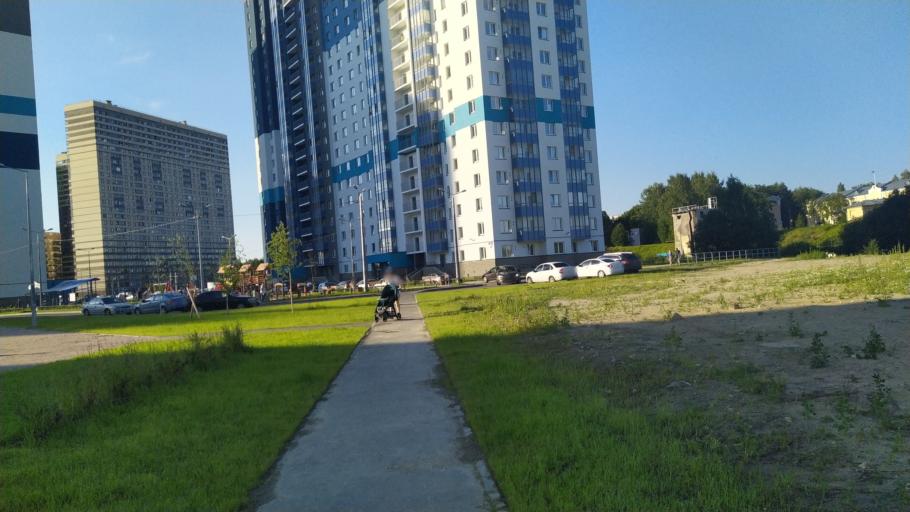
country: RU
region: Leningrad
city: Murino
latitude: 60.0355
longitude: 30.4589
